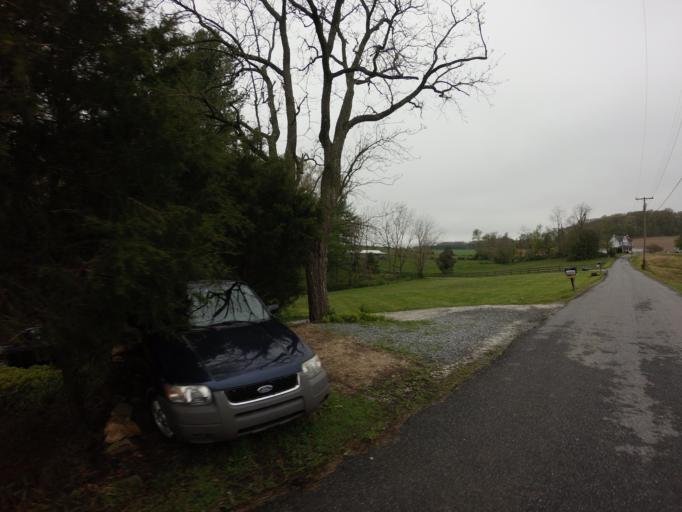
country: US
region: Maryland
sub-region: Carroll County
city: Hampstead
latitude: 39.5763
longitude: -76.7633
